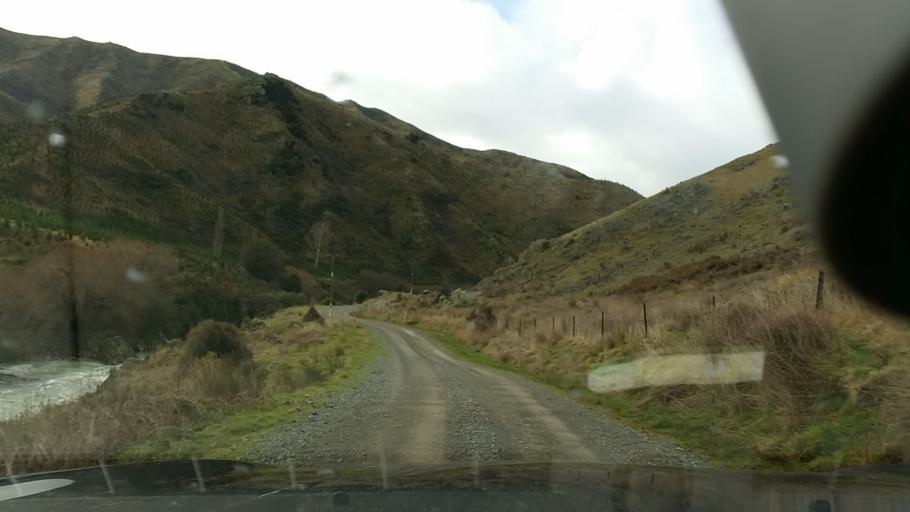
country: NZ
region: Tasman
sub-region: Tasman District
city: Richmond
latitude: -41.7310
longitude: 173.4411
